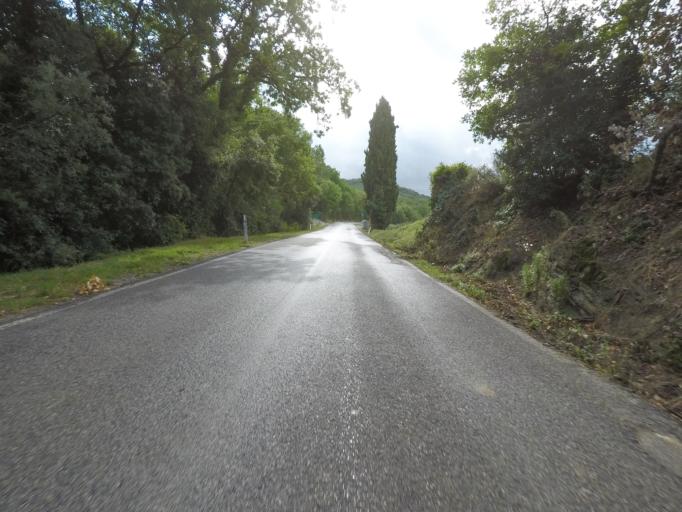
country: IT
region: Tuscany
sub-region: Provincia di Siena
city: Radda in Chianti
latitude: 43.4137
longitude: 11.3505
